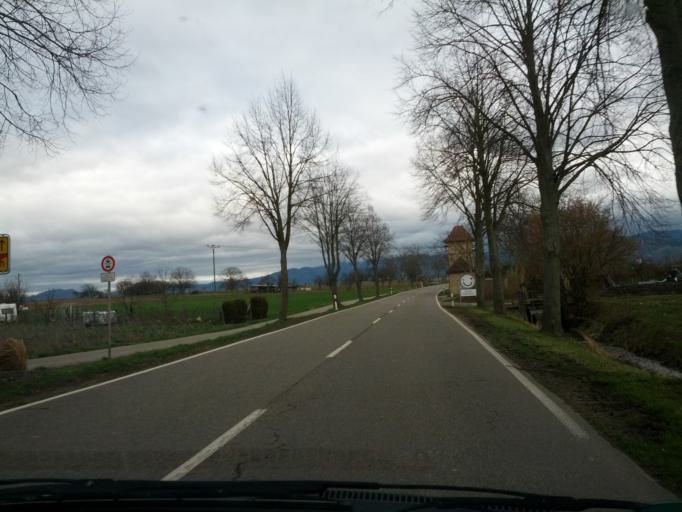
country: DE
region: Baden-Wuerttemberg
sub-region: Freiburg Region
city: Eschbach
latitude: 47.8892
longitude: 7.6618
